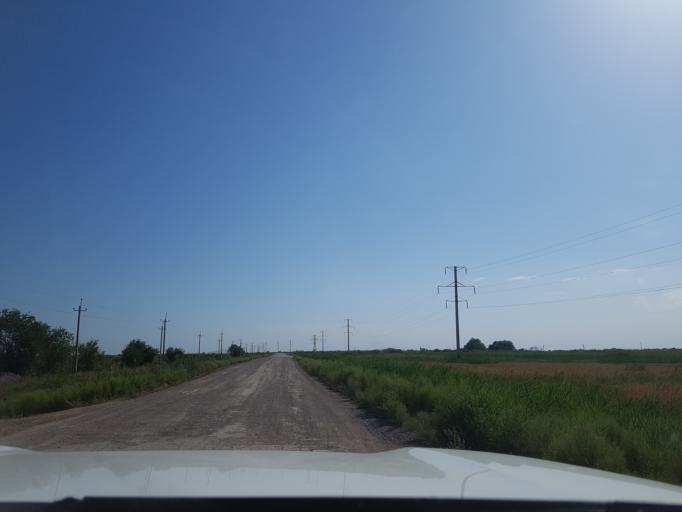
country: TM
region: Dasoguz
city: Koeneuergench
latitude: 42.1364
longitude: 58.9545
